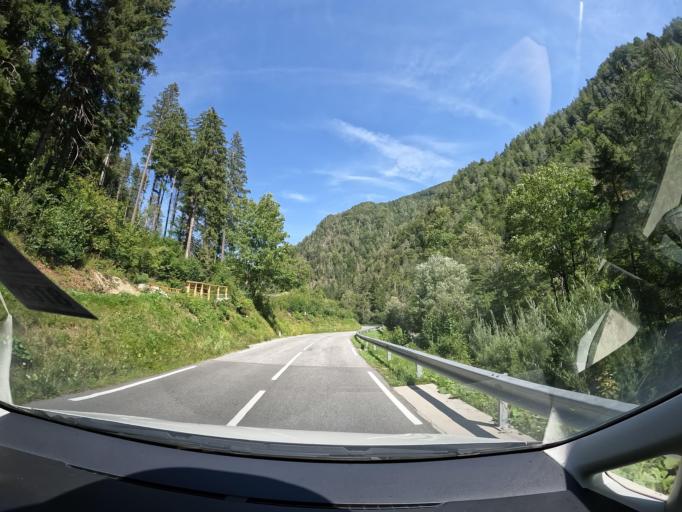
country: SI
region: Jesenice
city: Koroska Bela
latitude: 46.4472
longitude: 14.1529
